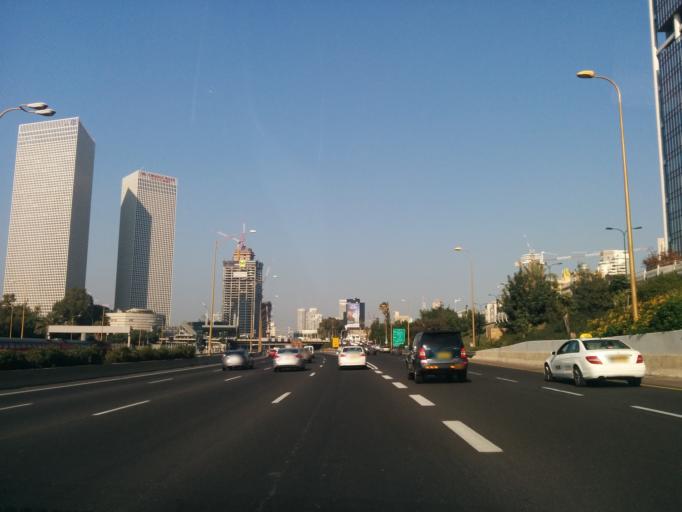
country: IL
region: Tel Aviv
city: Tel Aviv
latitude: 32.0693
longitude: 34.7932
